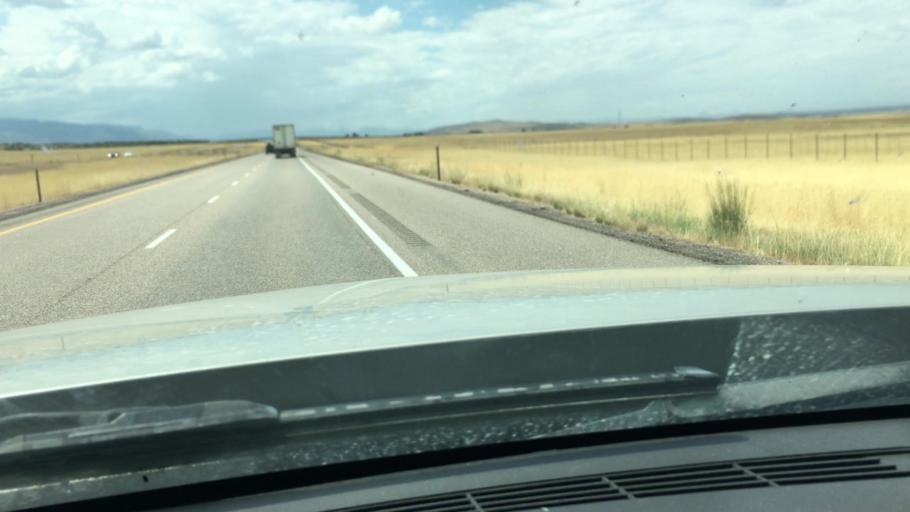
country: US
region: Utah
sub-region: Millard County
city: Fillmore
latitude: 39.1263
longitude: -112.2458
